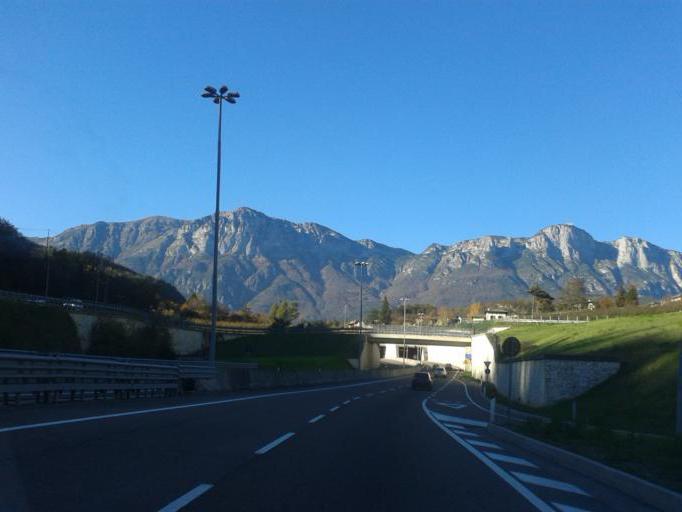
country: IT
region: Trentino-Alto Adige
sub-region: Provincia di Trento
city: Cadine
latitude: 46.0850
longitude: 11.0711
